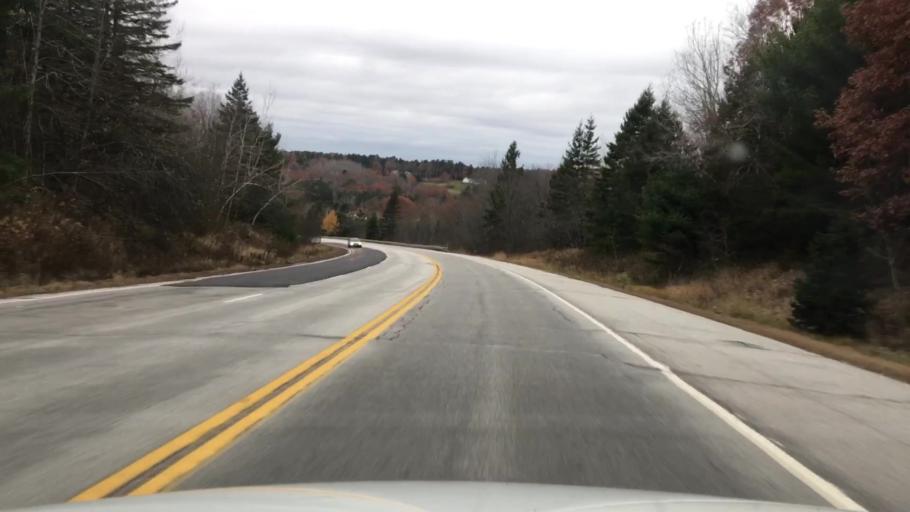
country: US
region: Maine
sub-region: Hancock County
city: Orland
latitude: 44.5762
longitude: -68.7354
